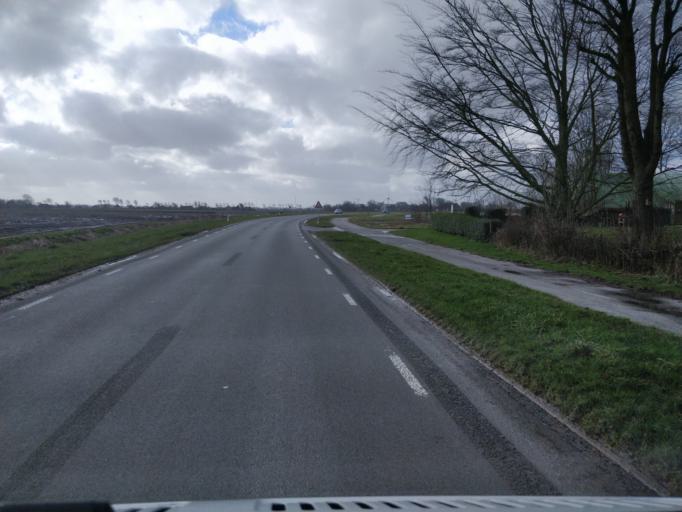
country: NL
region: Friesland
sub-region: Gemeente Franekeradeel
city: Sexbierum
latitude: 53.2073
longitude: 5.4617
